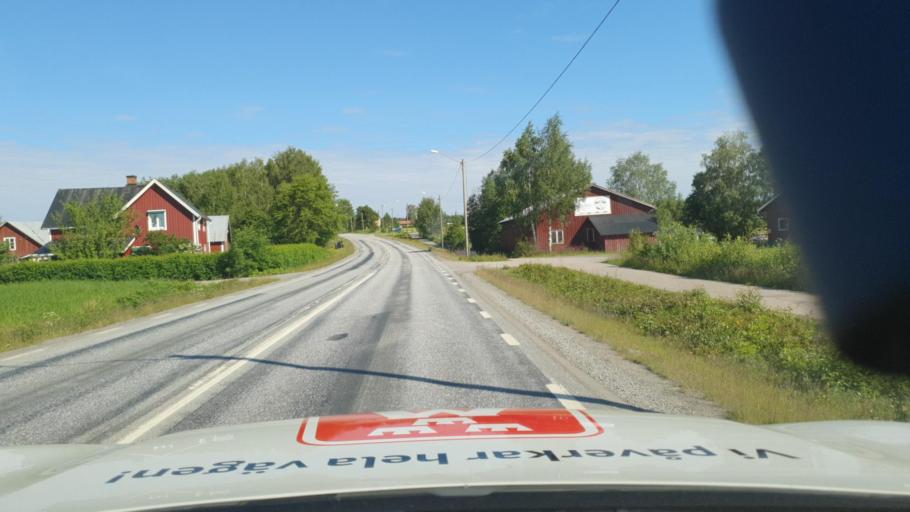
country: SE
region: Vaesterbotten
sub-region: Vannas Kommun
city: Vannasby
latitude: 64.0250
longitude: 20.0234
